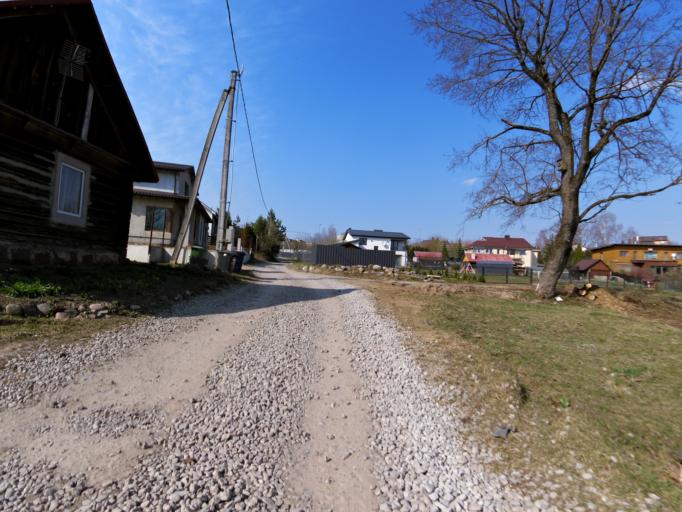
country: LT
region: Vilnius County
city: Pilaite
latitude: 54.6974
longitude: 25.1717
